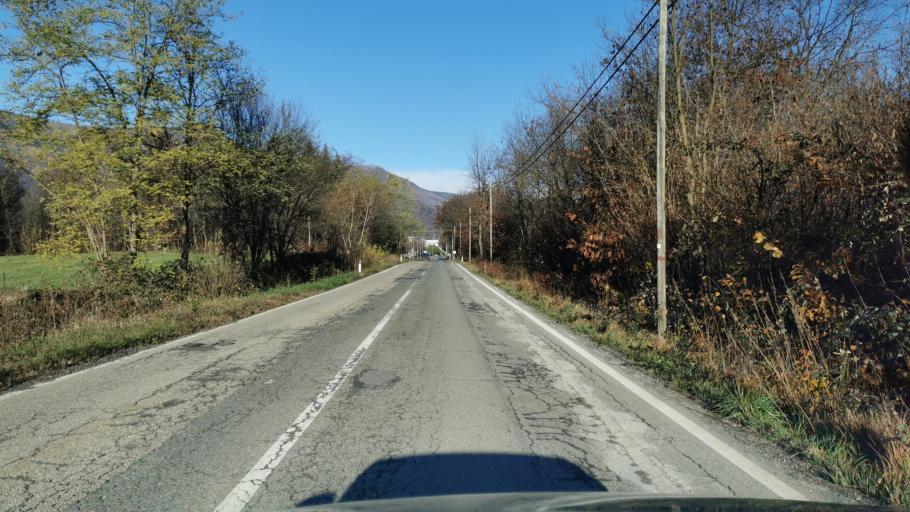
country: IT
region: Piedmont
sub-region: Provincia di Torino
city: La Cassa
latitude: 45.1662
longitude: 7.5257
